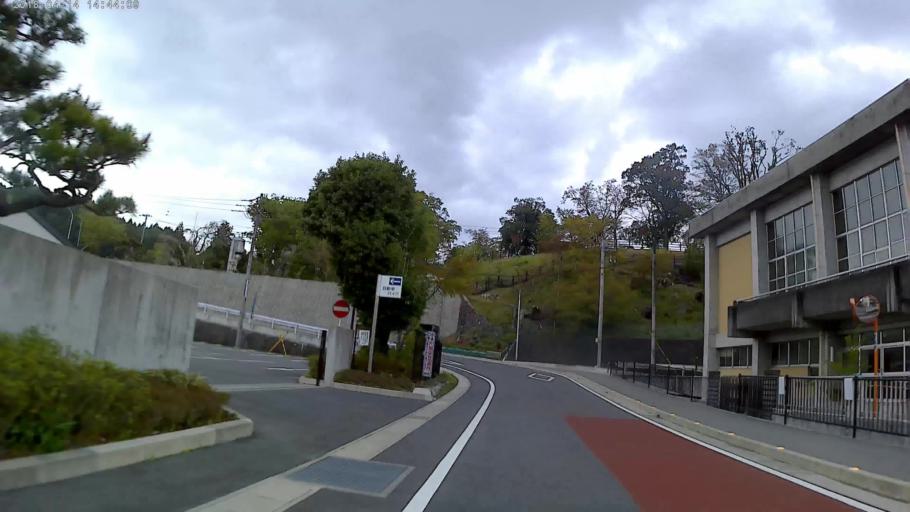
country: JP
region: Shizuoka
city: Gotemba
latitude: 35.3613
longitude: 138.9869
